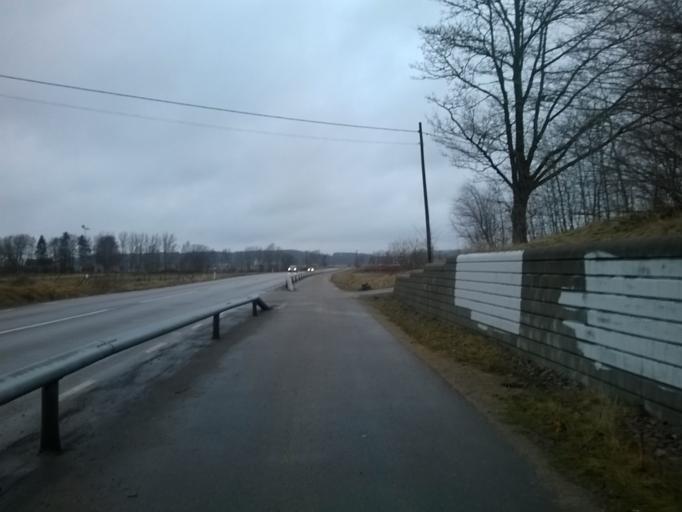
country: SE
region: Vaestra Goetaland
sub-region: Kungalvs Kommun
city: Kungalv
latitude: 57.8996
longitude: 11.9313
